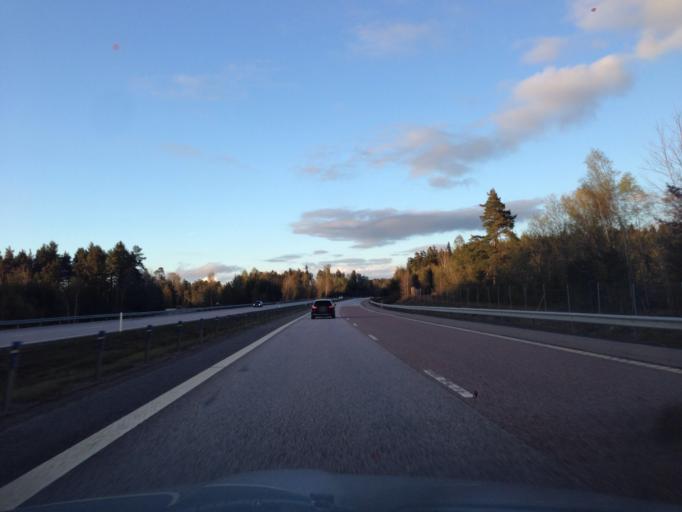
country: SE
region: Soedermanland
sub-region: Trosa Kommun
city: Vagnharad
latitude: 58.9282
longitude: 17.3978
